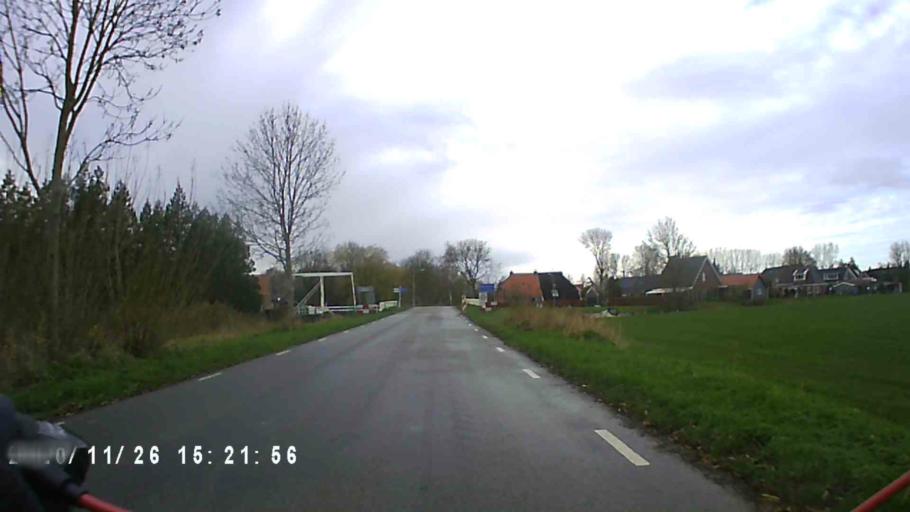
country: NL
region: Groningen
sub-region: Gemeente Appingedam
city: Appingedam
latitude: 53.3145
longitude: 6.7884
